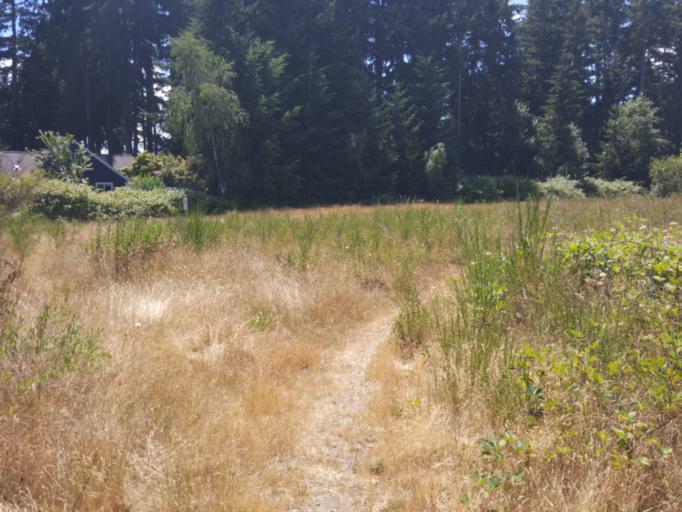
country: US
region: Washington
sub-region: Pierce County
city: Fircrest
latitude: 47.2187
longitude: -122.5292
